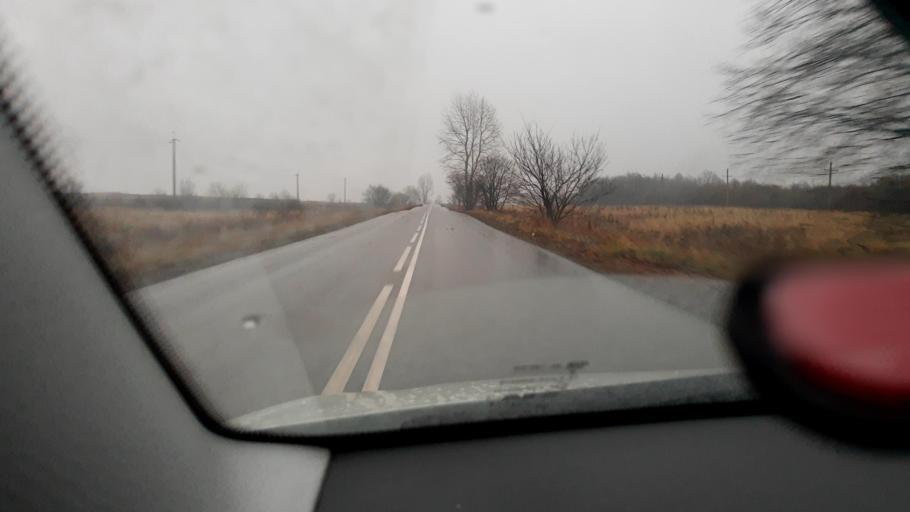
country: RU
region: Bashkortostan
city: Iglino
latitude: 54.8995
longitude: 56.2523
